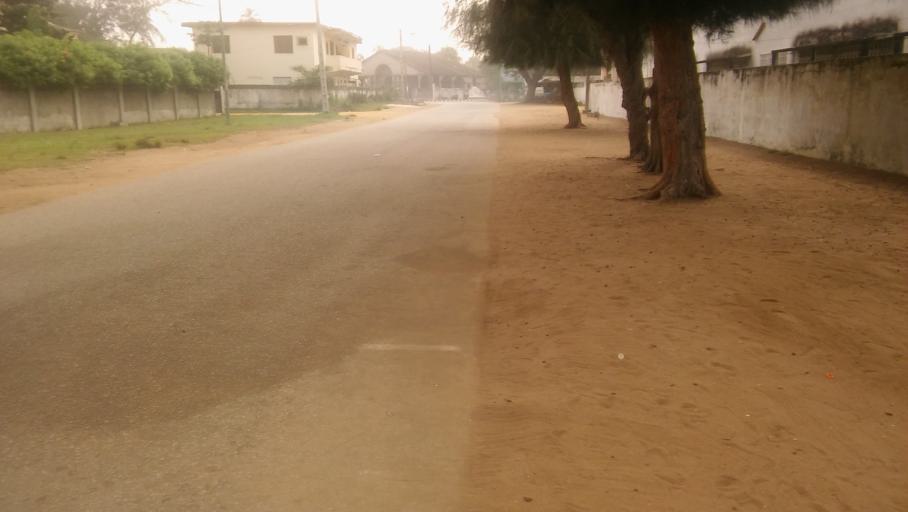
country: CI
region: Sud-Comoe
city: Grand-Bassam
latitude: 5.1949
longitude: -3.7338
